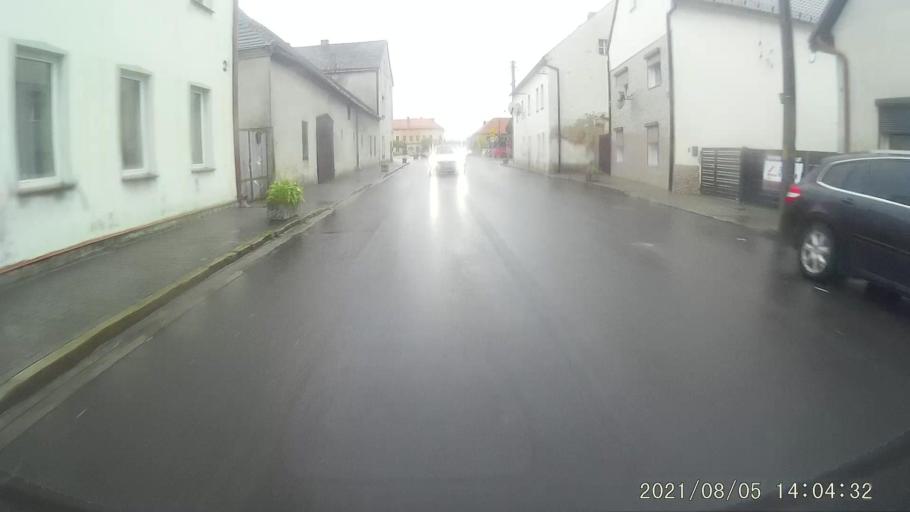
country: PL
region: Opole Voivodeship
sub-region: Powiat krapkowicki
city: Strzeleczki
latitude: 50.4607
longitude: 17.8533
